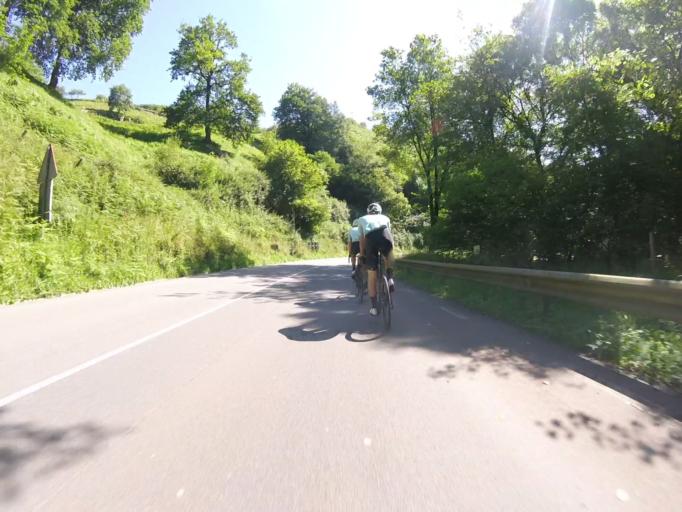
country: ES
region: Basque Country
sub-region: Provincia de Guipuzcoa
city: Tolosa
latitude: 43.1239
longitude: -2.0968
